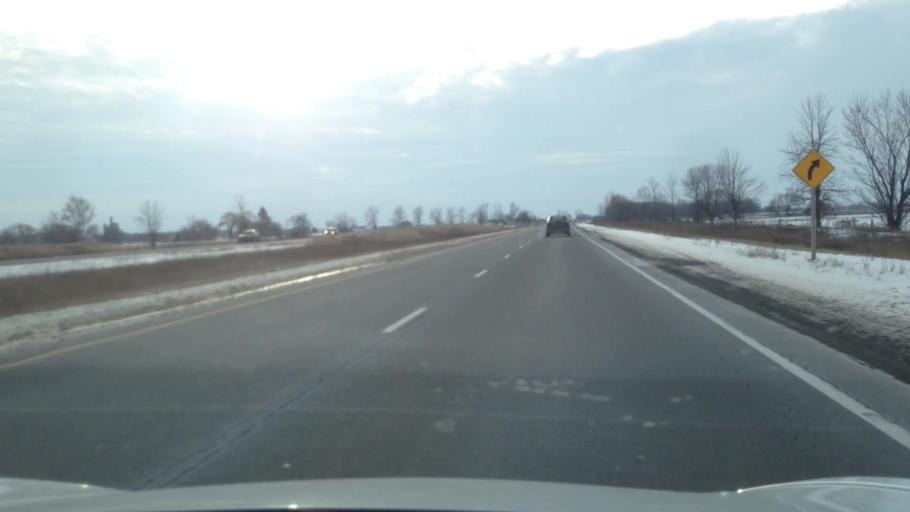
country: CA
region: Ontario
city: Casselman
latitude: 45.3190
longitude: -75.0157
